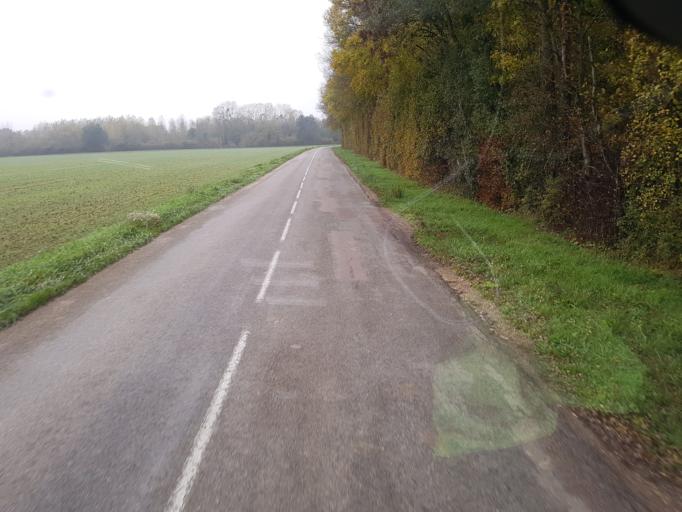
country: FR
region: Bourgogne
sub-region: Departement de la Cote-d'Or
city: Genlis
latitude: 47.2958
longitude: 5.2195
